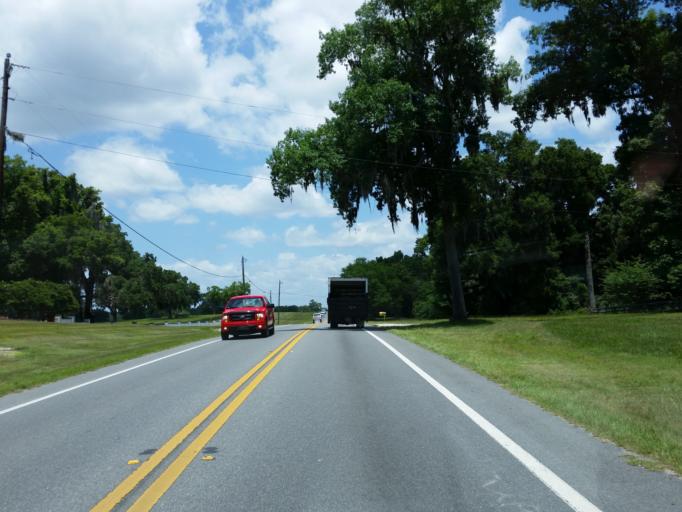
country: US
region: Florida
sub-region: Marion County
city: Belleview
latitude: 28.9908
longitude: -82.0413
